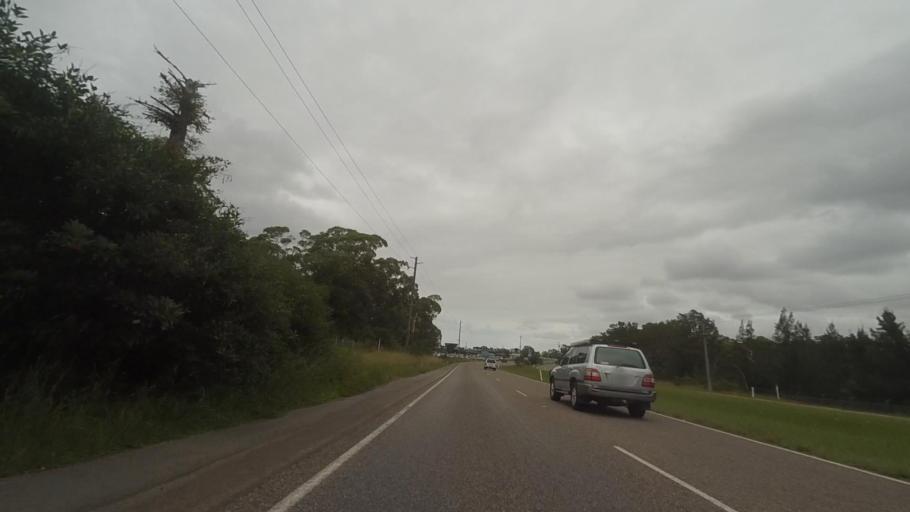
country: AU
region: New South Wales
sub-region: Wyong Shire
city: Buff Point
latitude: -33.1944
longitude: 151.5268
